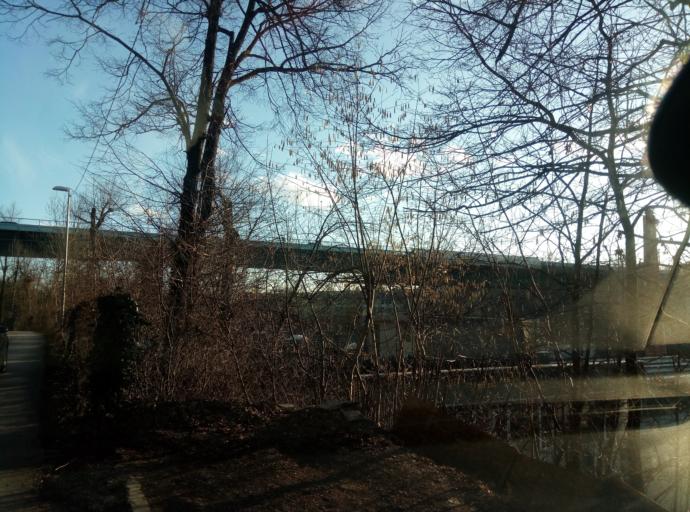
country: SI
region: Kranj
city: Kranj
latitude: 46.2301
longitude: 14.3634
